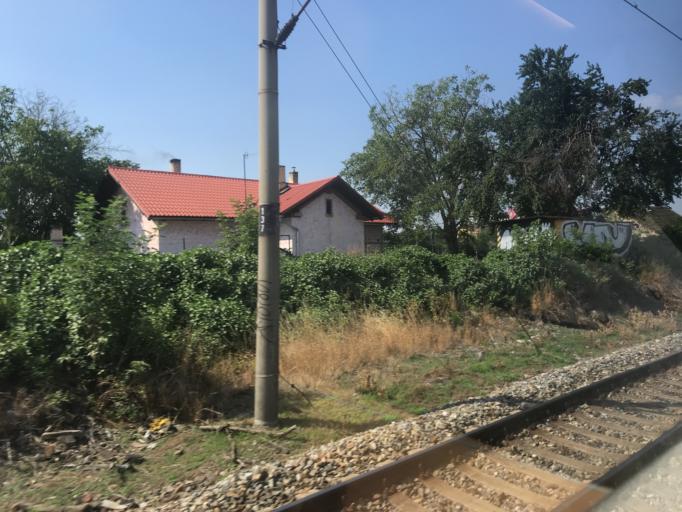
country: CZ
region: Praha
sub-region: Praha 8
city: Karlin
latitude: 50.0659
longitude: 14.4796
